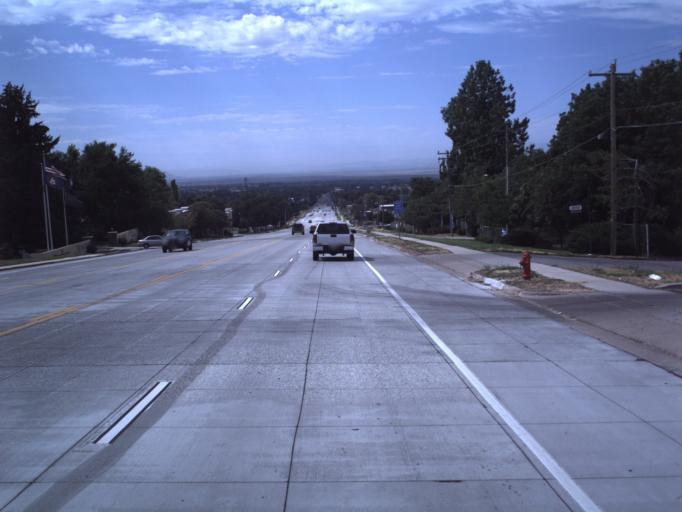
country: US
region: Utah
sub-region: Davis County
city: Hill Air Force Bace
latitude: 41.1012
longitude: -111.9735
